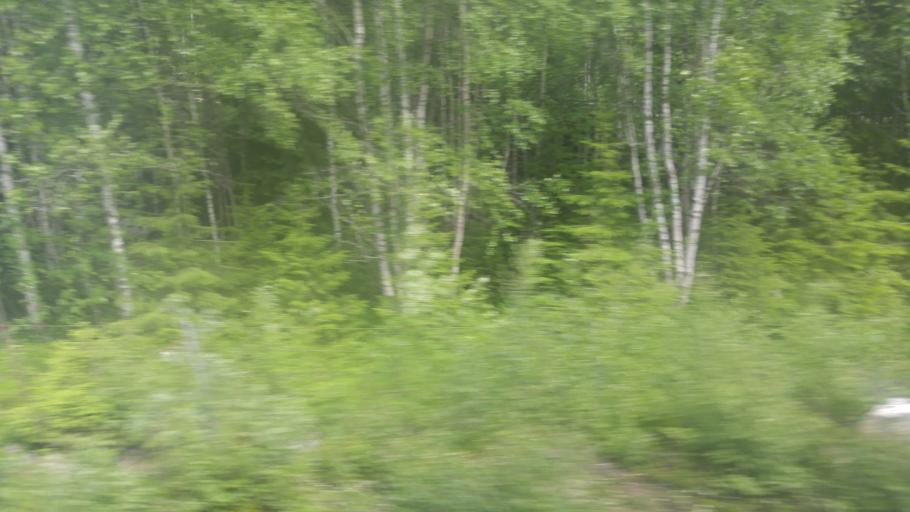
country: NO
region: Sor-Trondelag
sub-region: Selbu
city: Mebonden
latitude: 62.9585
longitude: 10.8113
